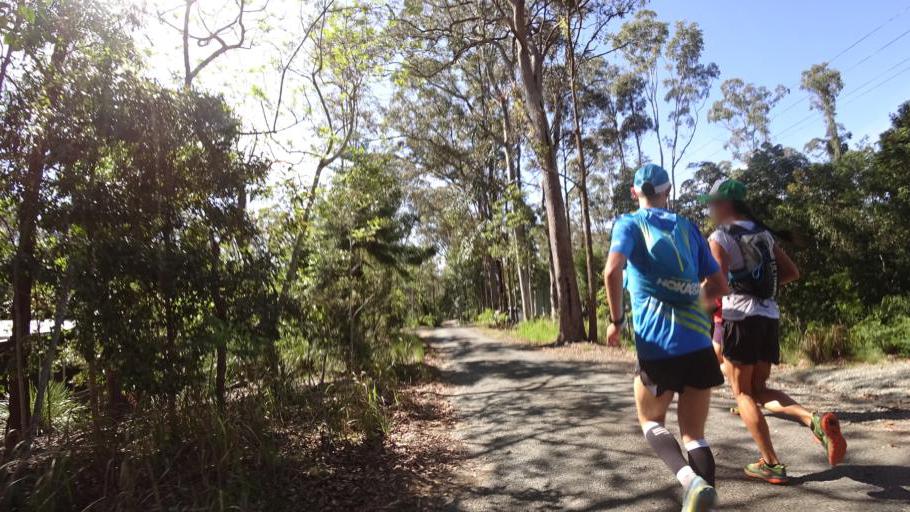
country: AU
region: Queensland
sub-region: Moreton Bay
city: Highvale
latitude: -27.4006
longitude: 152.7824
